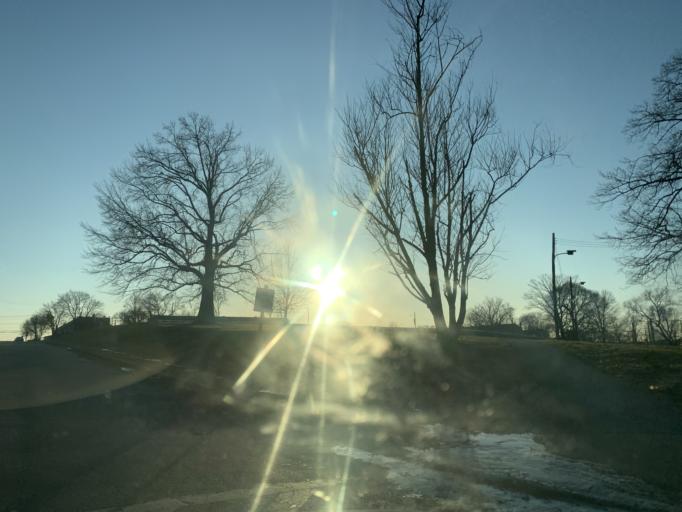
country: US
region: Maryland
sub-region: Baltimore County
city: Lansdowne
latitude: 39.2628
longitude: -76.6378
